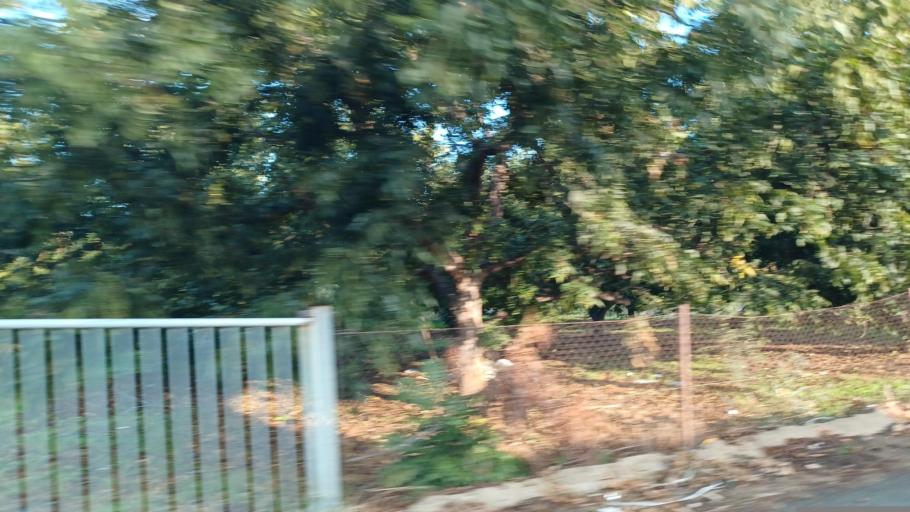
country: CY
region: Pafos
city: Kissonerga
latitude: 34.8294
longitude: 32.4045
